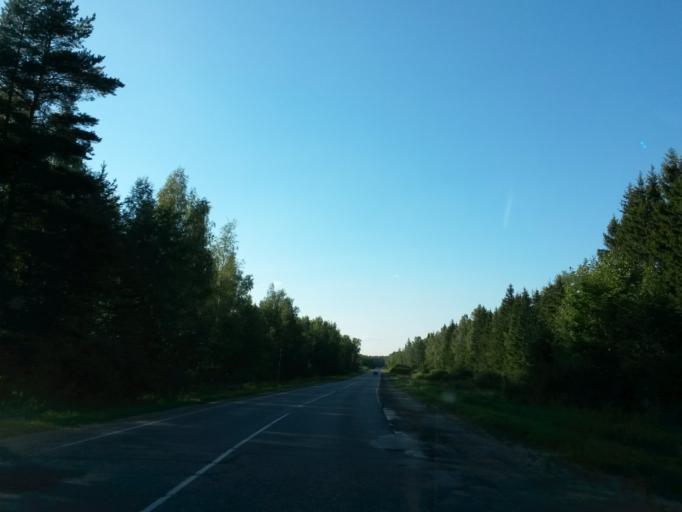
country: RU
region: Ivanovo
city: Pistsovo
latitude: 57.0918
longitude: 40.6630
